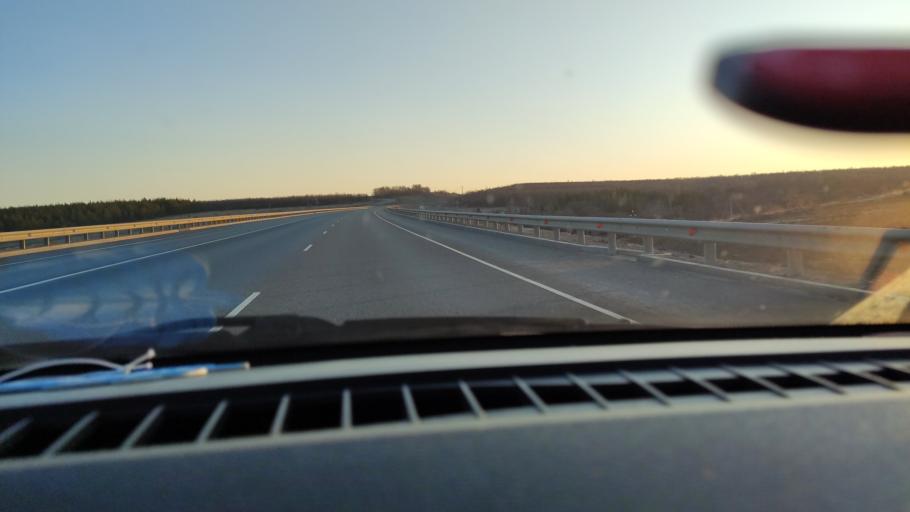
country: RU
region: Saratov
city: Yelshanka
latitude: 51.8787
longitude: 46.5083
